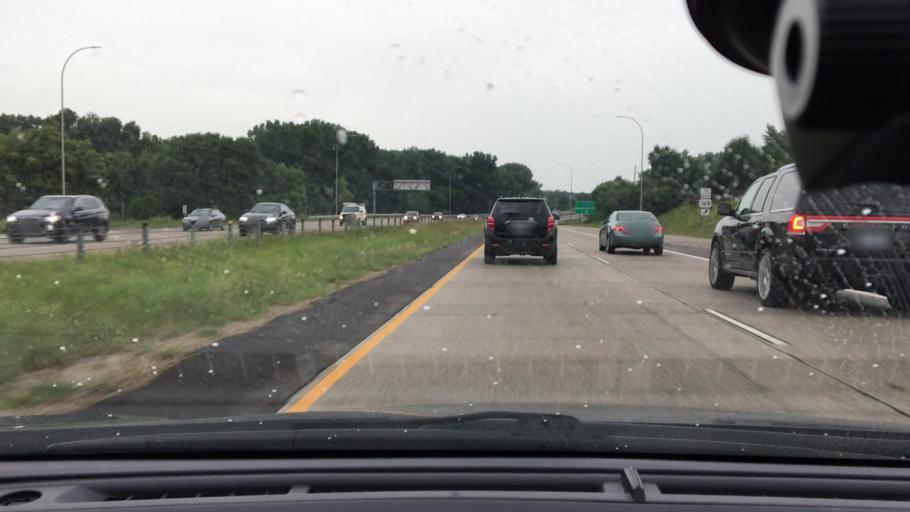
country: US
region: Minnesota
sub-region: Hennepin County
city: Minnetonka Mills
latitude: 44.9415
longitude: -93.3983
